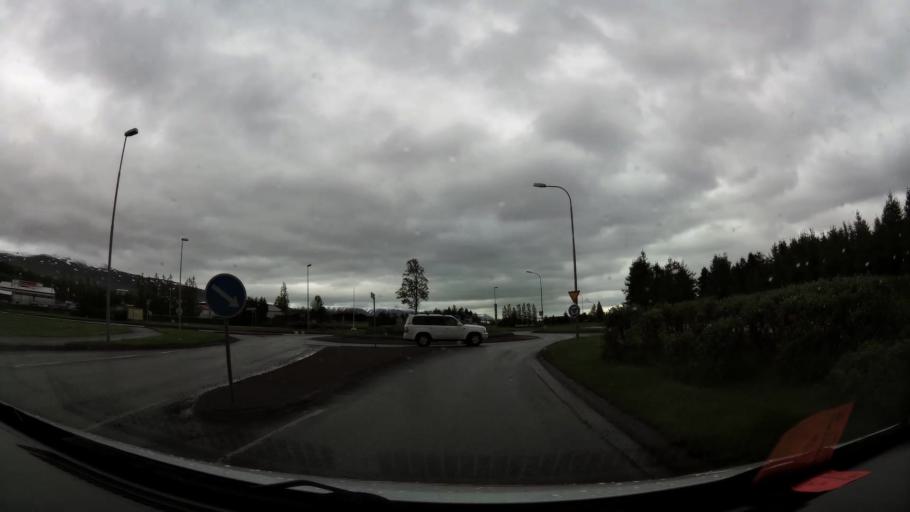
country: IS
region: Northeast
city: Akureyri
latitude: 65.6790
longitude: -18.1316
